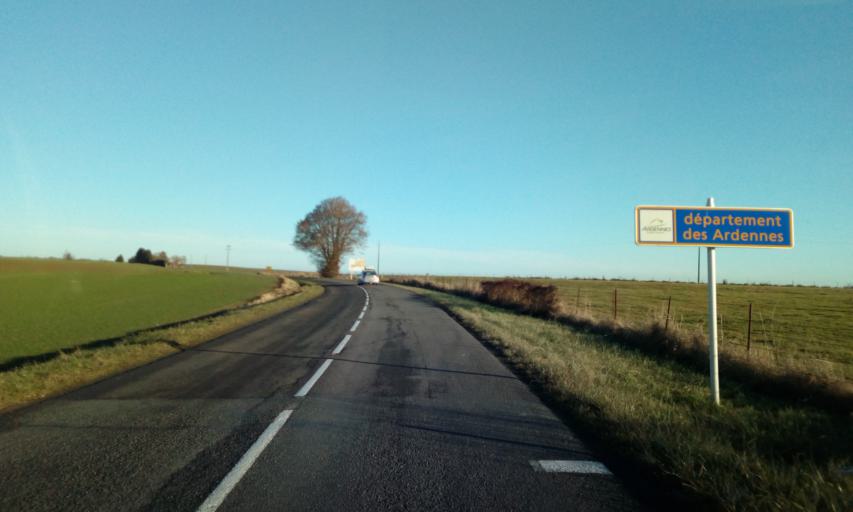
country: FR
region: Picardie
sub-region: Departement de l'Aisne
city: Rozoy-sur-Serre
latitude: 49.6967
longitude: 4.1753
